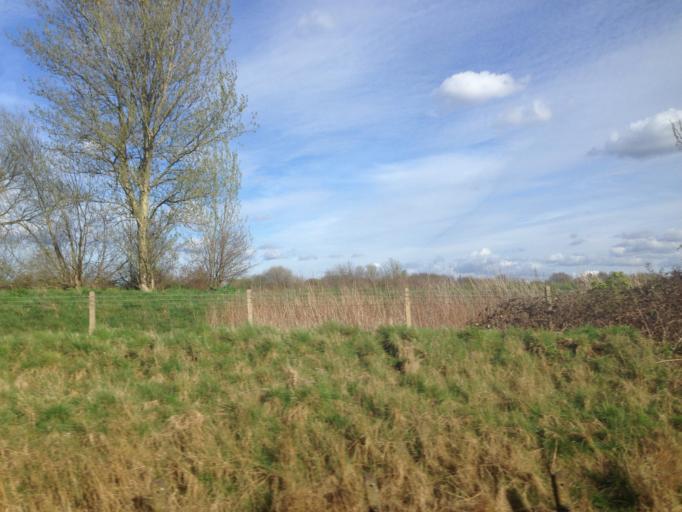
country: GB
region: England
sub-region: Greater London
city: Mitcham
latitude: 51.4014
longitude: -0.1583
